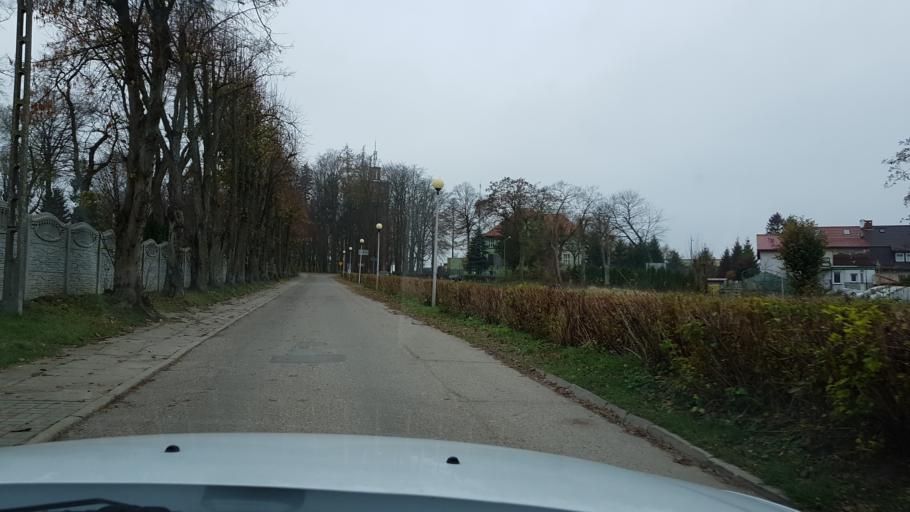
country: PL
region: West Pomeranian Voivodeship
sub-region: Powiat slawienski
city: Darlowo
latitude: 54.4257
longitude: 16.4185
